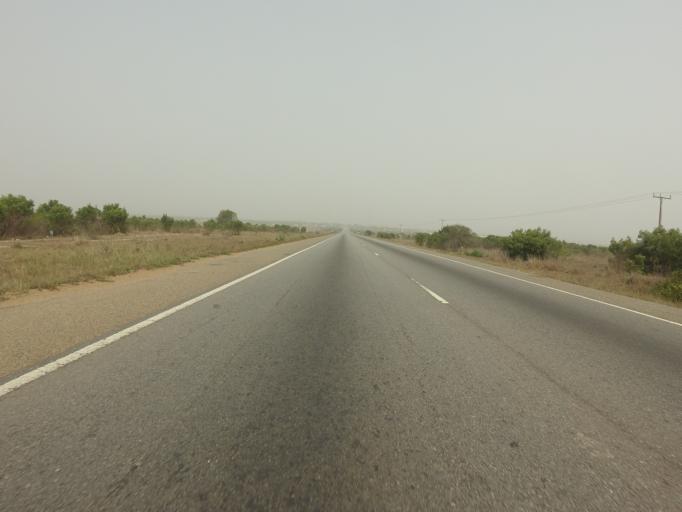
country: GH
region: Greater Accra
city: Tema
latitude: 5.8602
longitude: 0.2763
